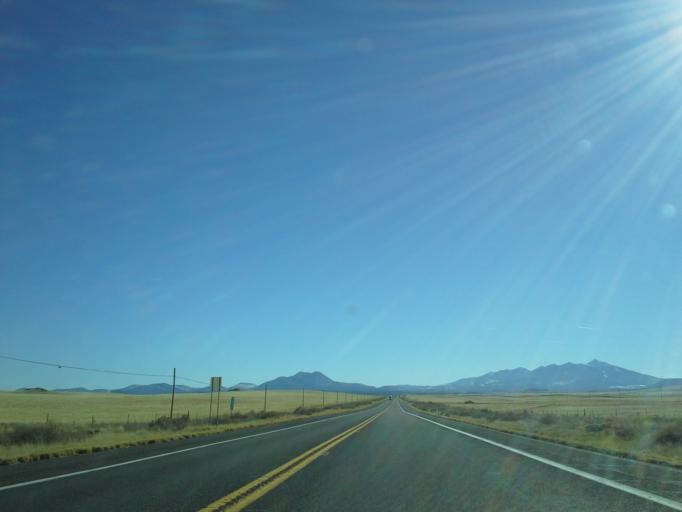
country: US
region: Arizona
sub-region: Coconino County
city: Flagstaff
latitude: 35.6216
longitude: -111.5218
